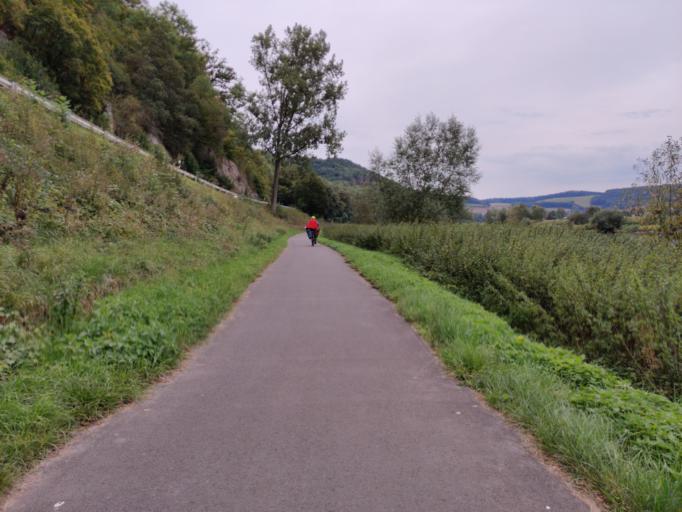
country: DE
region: Lower Saxony
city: Pegestorf
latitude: 51.9192
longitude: 9.4619
